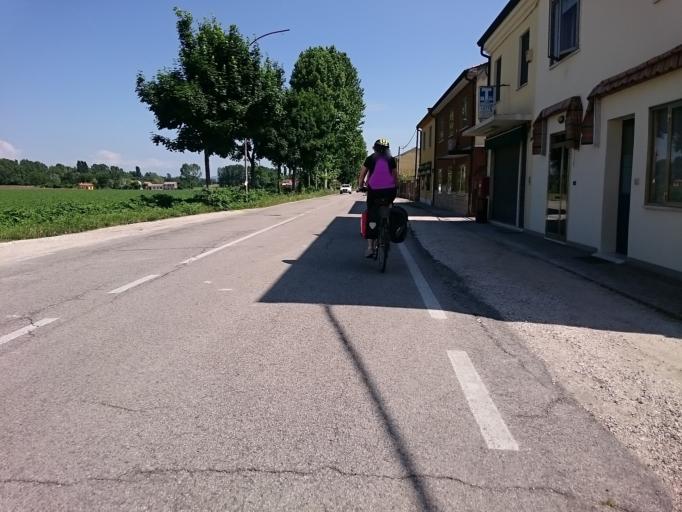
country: IT
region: Veneto
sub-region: Provincia di Padova
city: Montagnana
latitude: 45.2381
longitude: 11.4715
